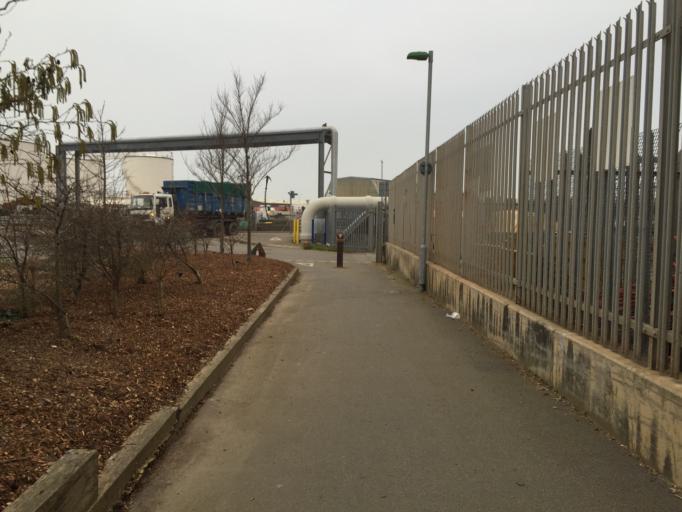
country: JE
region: St Helier
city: Saint Helier
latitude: 49.1740
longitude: -2.1086
